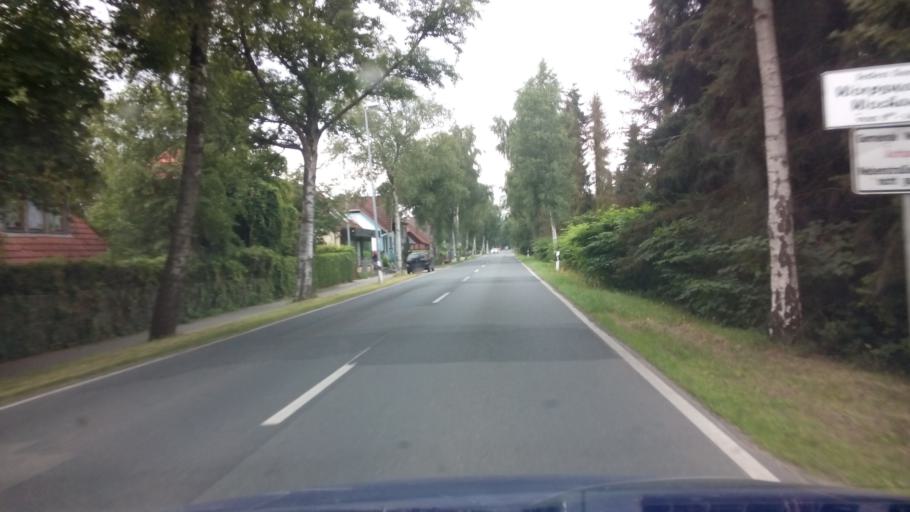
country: DE
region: Lower Saxony
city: Worpswede
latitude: 53.2038
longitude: 8.9315
